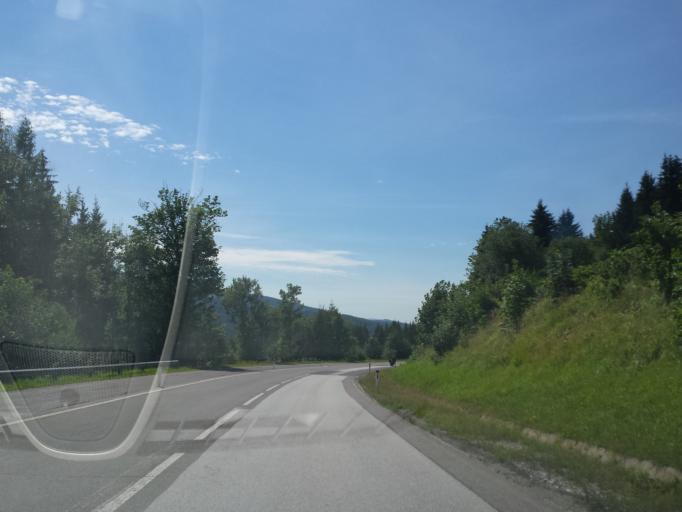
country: AT
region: Lower Austria
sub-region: Politischer Bezirk Neunkirchen
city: Semmering
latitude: 47.6308
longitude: 15.8180
